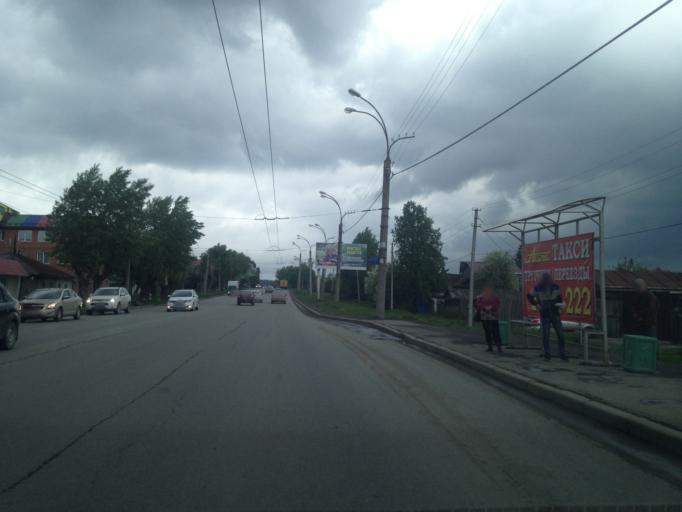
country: RU
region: Sverdlovsk
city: Istok
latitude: 56.7496
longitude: 60.6806
